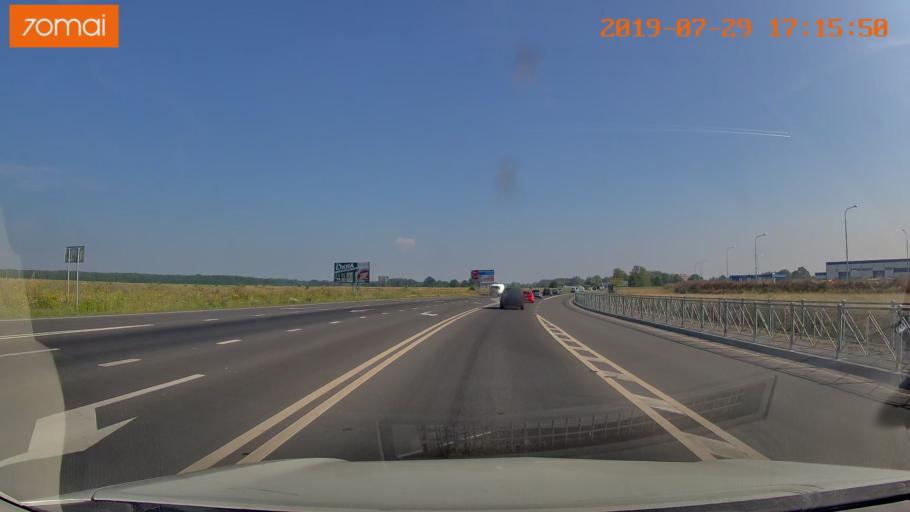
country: RU
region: Kaliningrad
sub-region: Gorod Kaliningrad
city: Kaliningrad
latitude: 54.7829
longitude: 20.4128
